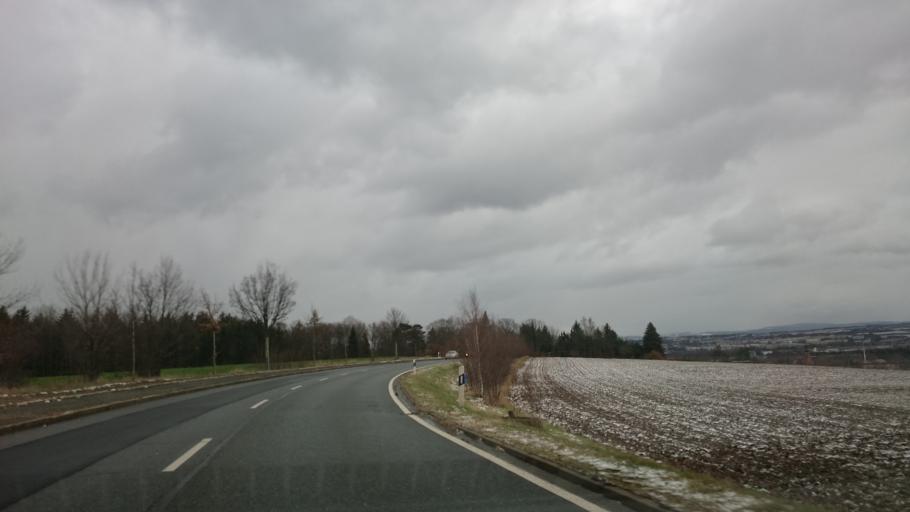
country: DE
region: Saxony
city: Weissenborn
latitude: 50.7299
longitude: 12.4516
